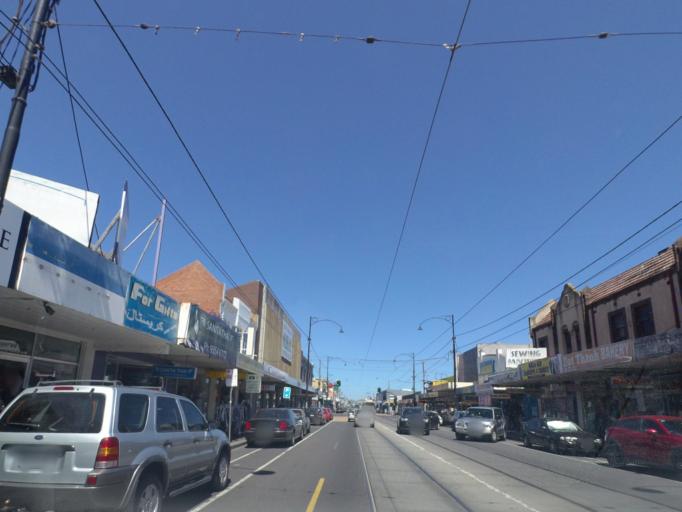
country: AU
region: Victoria
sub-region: Moreland
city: Coburg
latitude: -37.7442
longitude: 144.9660
